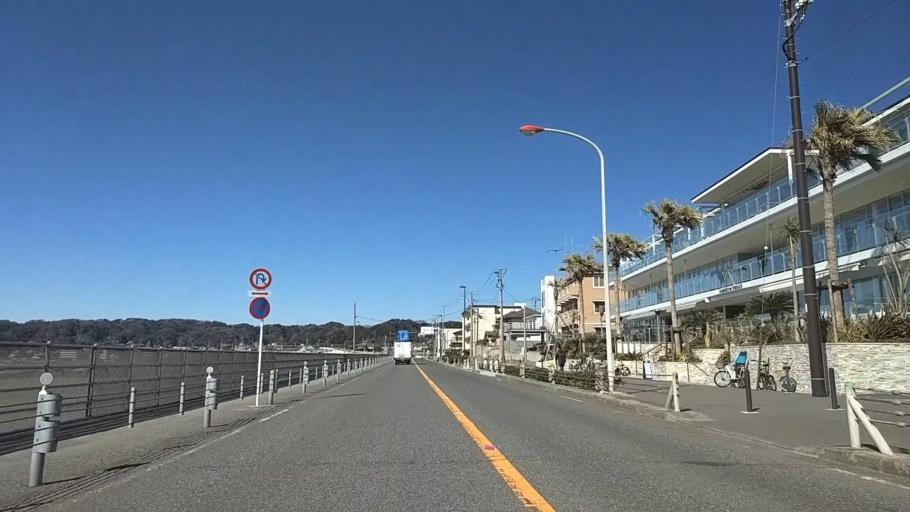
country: JP
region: Kanagawa
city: Kamakura
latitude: 35.3071
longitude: 139.5483
